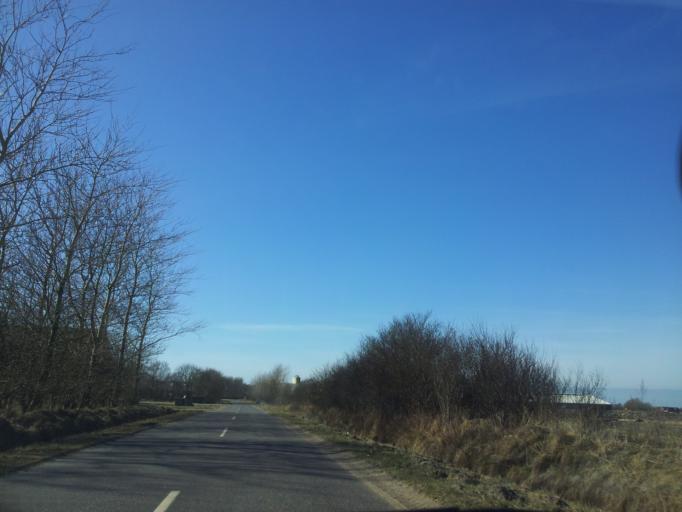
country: DK
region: South Denmark
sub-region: Tonder Kommune
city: Sherrebek
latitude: 55.1731
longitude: 8.7271
